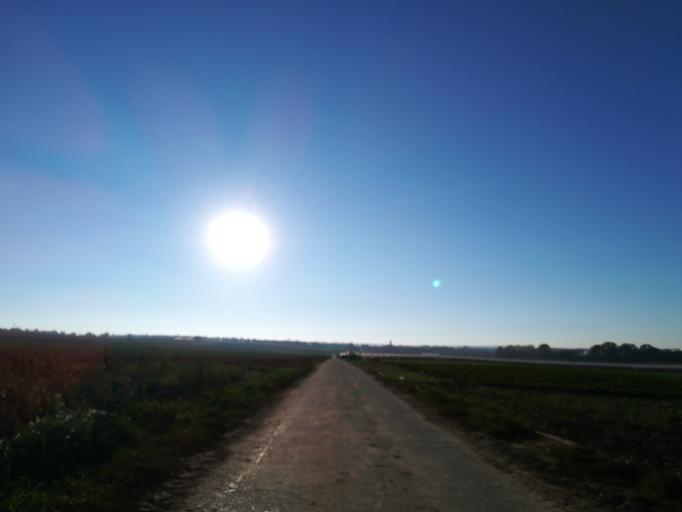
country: DE
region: Baden-Wuerttemberg
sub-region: Regierungsbezirk Stuttgart
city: Neuhausen auf den Fildern
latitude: 48.6772
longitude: 9.2646
